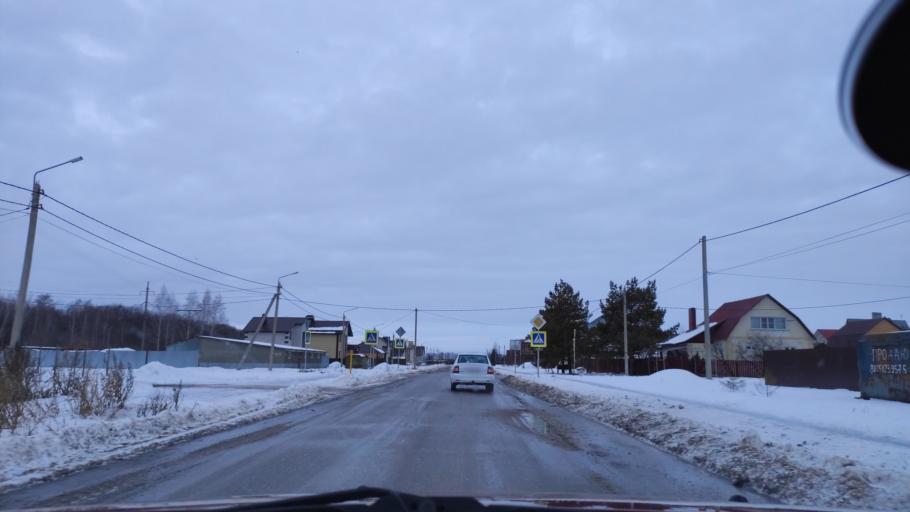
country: RU
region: Tambov
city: Tambov
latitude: 52.7595
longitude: 41.3677
